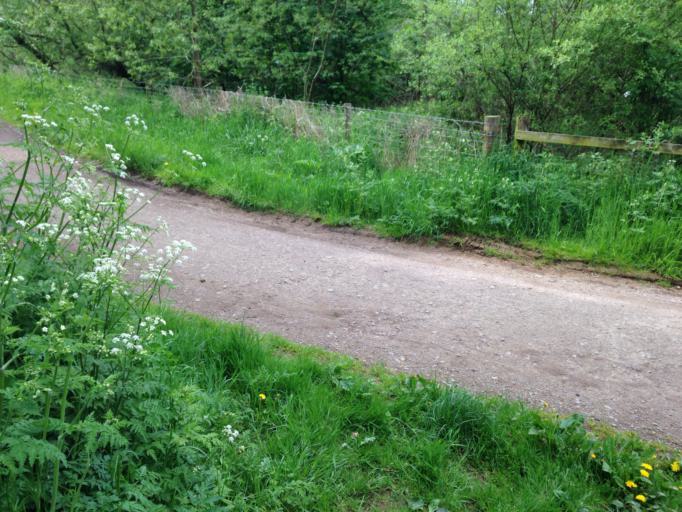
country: GB
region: England
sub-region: Northamptonshire
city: Brixworth
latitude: 52.3140
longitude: -0.8566
